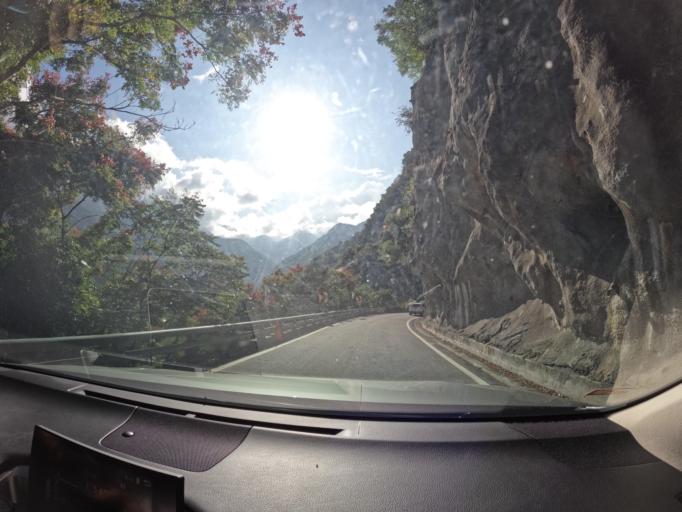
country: TW
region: Taiwan
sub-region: Taitung
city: Taitung
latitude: 23.1773
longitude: 121.0402
